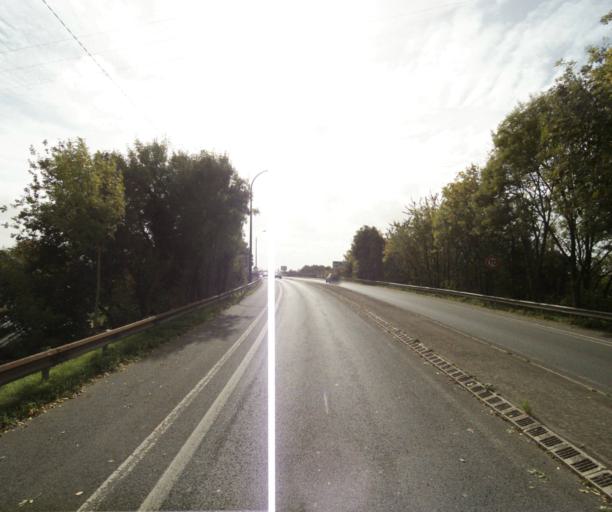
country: FR
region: Nord-Pas-de-Calais
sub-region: Departement du Nord
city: La Bassee
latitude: 50.5246
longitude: 2.8026
